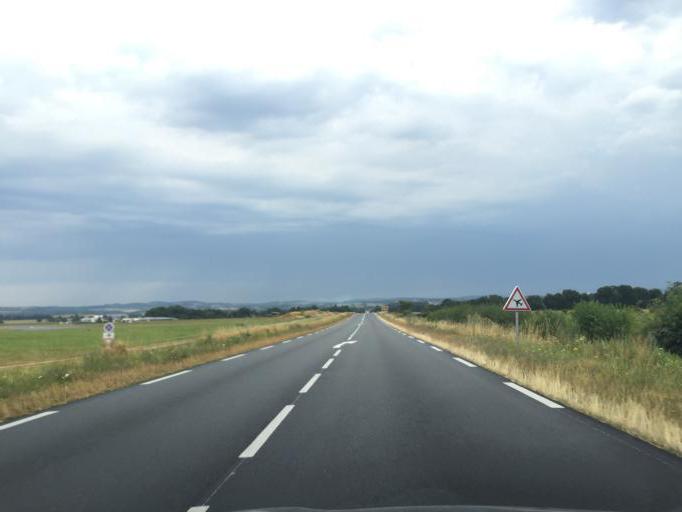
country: FR
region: Auvergne
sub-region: Departement de l'Allier
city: Lapalisse
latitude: 46.2490
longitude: 3.5790
